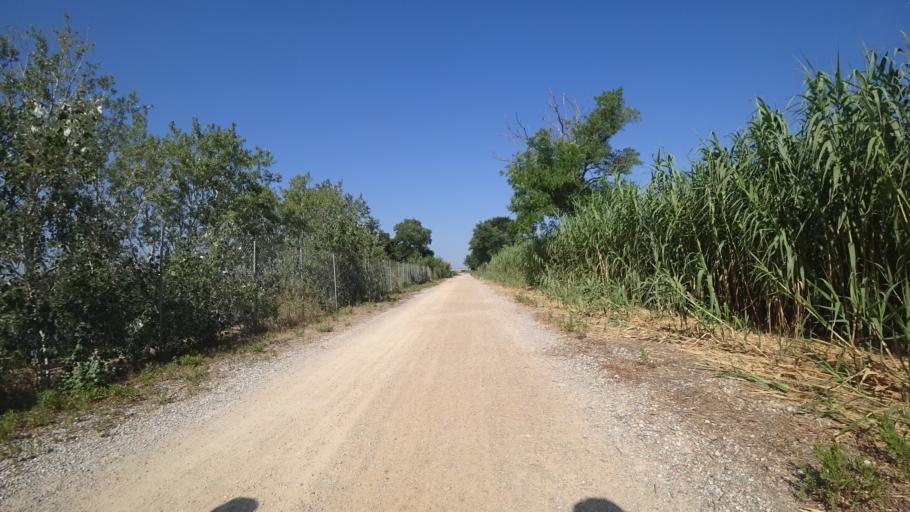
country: FR
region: Languedoc-Roussillon
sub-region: Departement des Pyrenees-Orientales
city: Le Barcares
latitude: 42.7702
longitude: 3.0209
